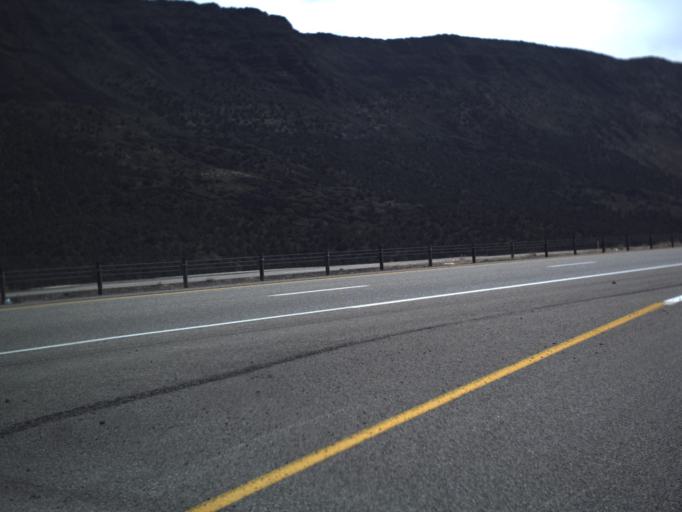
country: US
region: Utah
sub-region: Washington County
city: Toquerville
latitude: 37.4040
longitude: -113.2388
